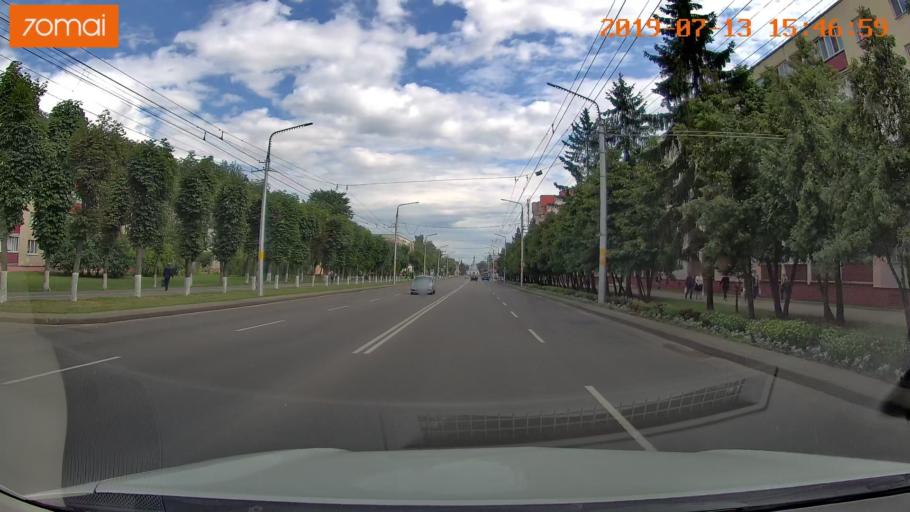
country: BY
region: Mogilev
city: Babruysk
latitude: 53.1501
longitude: 29.2275
